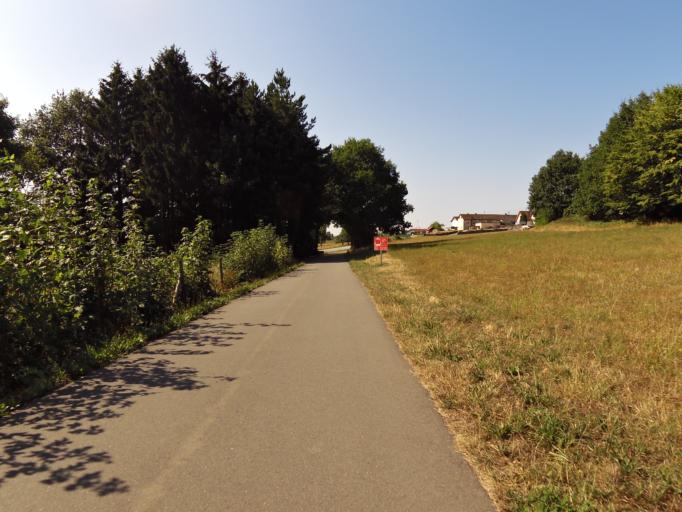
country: DE
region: Baden-Wuerttemberg
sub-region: Karlsruhe Region
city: Limbach
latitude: 49.4660
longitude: 9.2175
